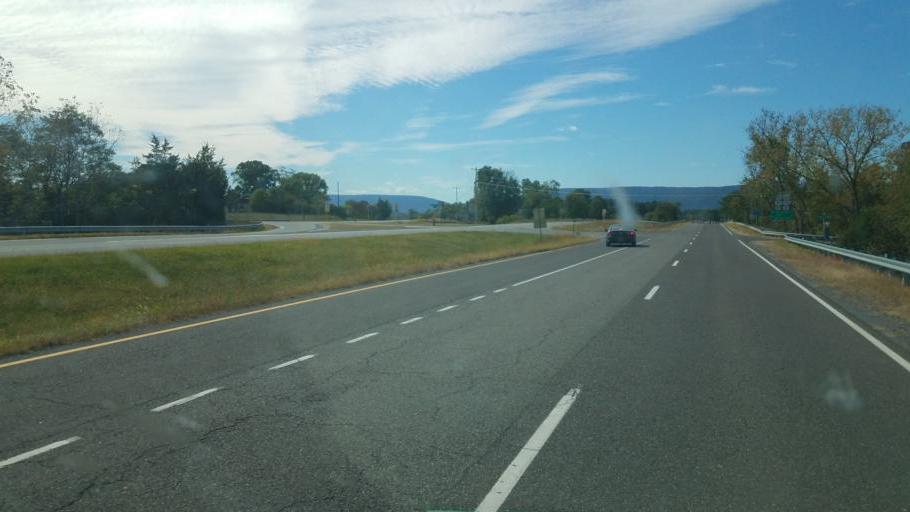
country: US
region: Virginia
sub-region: Page County
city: Luray
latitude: 38.6749
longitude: -78.4111
